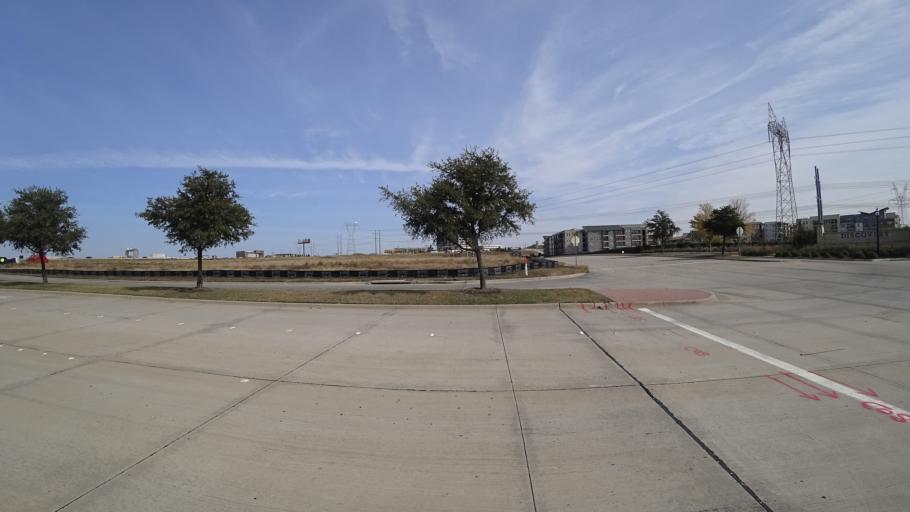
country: US
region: Texas
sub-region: Denton County
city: The Colony
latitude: 33.0576
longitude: -96.9004
